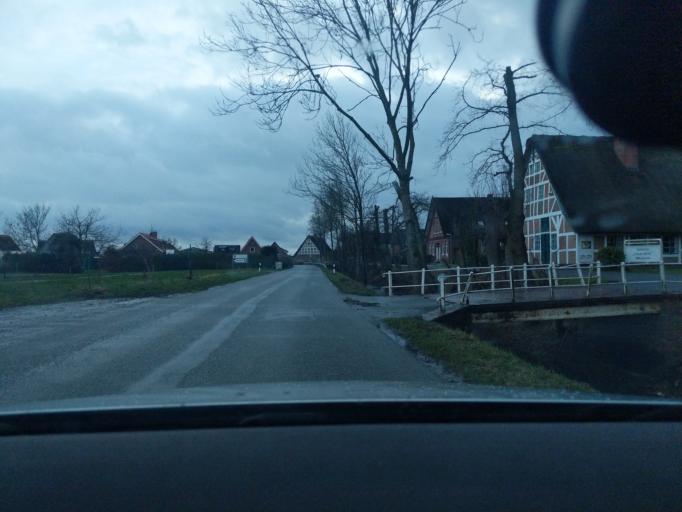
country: DE
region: Lower Saxony
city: Jork
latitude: 53.5350
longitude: 9.6527
